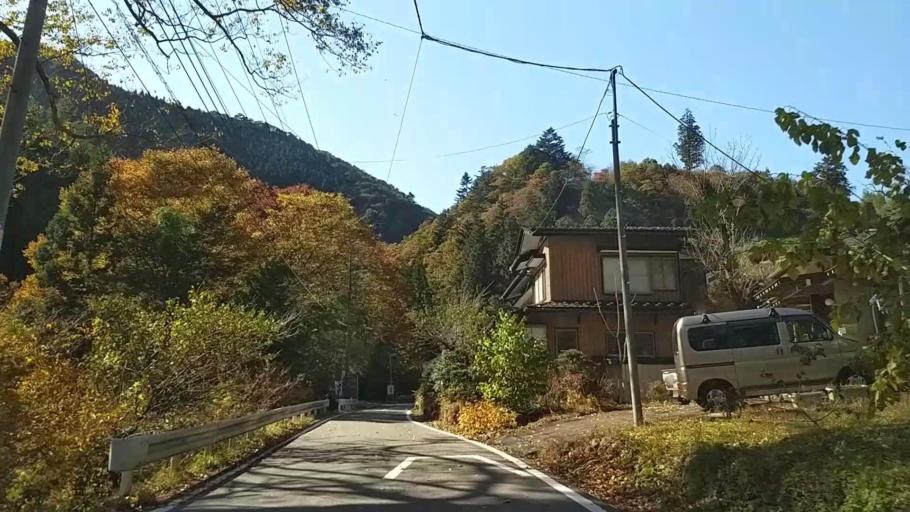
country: JP
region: Yamanashi
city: Uenohara
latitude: 35.7050
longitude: 139.0184
